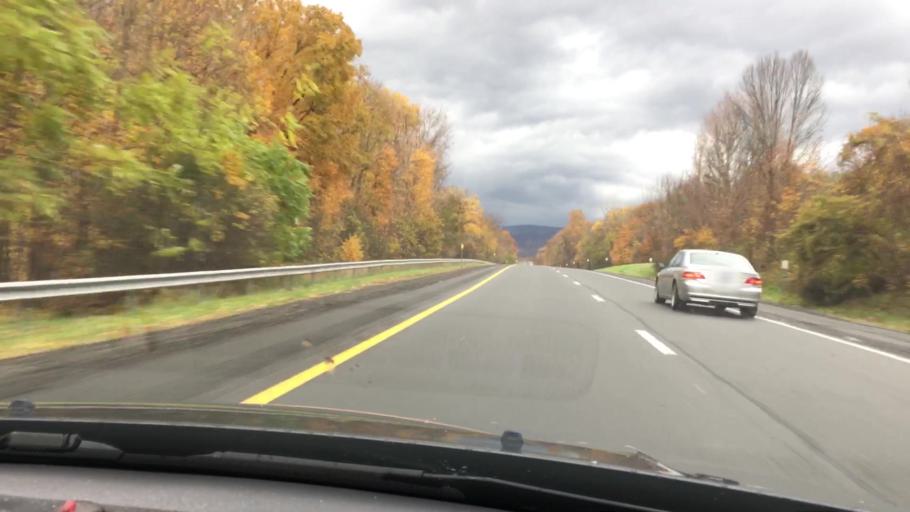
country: US
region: New York
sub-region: Orange County
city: Vails Gate
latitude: 41.4772
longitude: -74.0774
